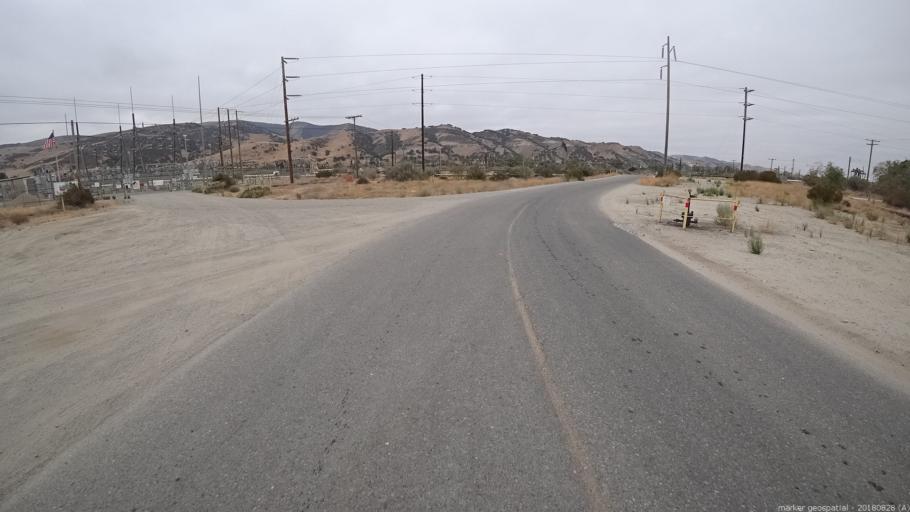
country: US
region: California
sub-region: San Luis Obispo County
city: Lake Nacimiento
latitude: 35.9525
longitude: -120.8681
